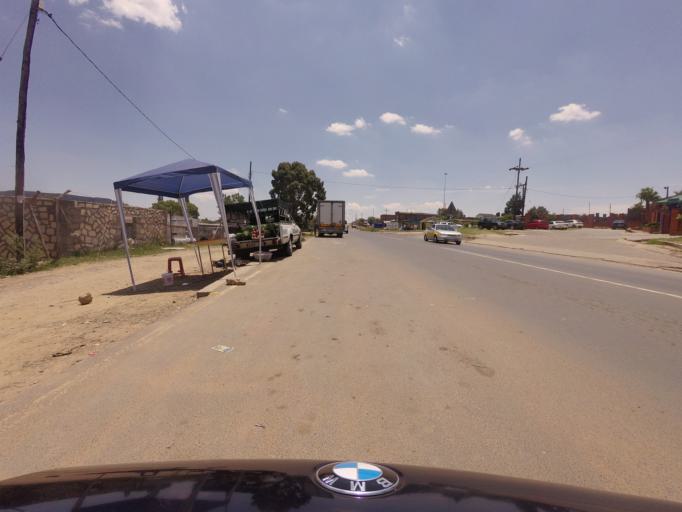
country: LS
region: Maseru
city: Maseru
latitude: -29.2785
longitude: 27.5288
